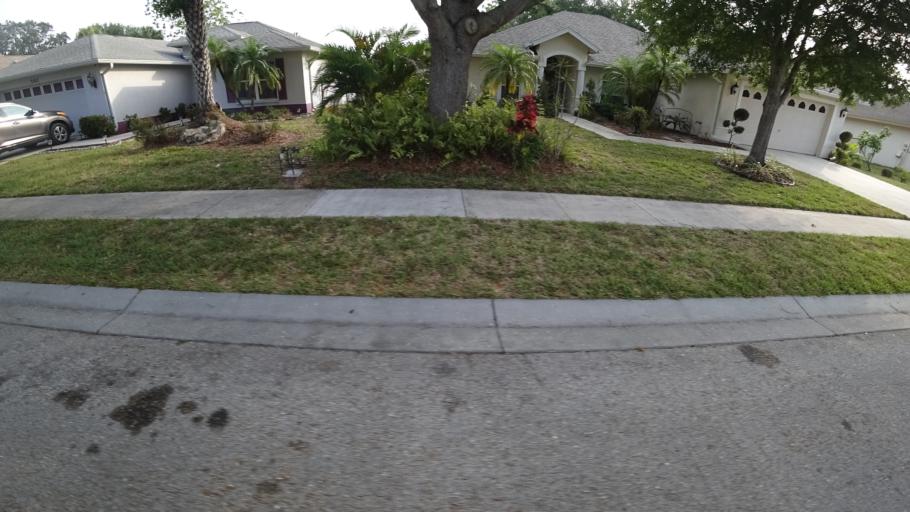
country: US
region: Florida
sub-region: Manatee County
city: Samoset
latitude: 27.4372
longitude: -82.5244
